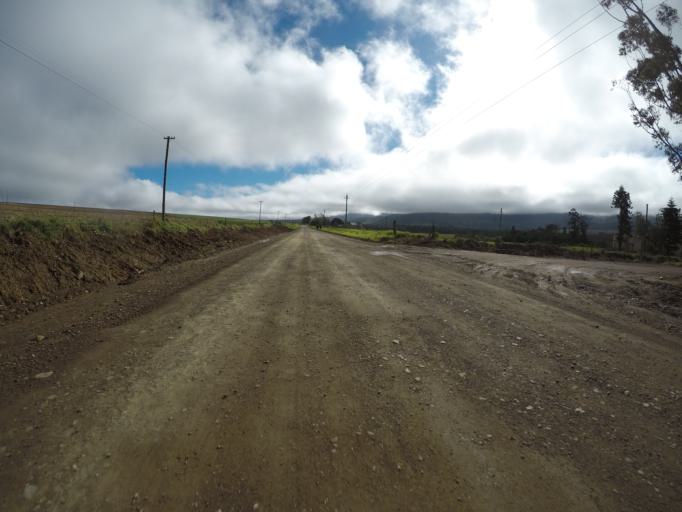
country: ZA
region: Western Cape
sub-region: Cape Winelands District Municipality
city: Ashton
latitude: -34.1337
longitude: 19.8565
